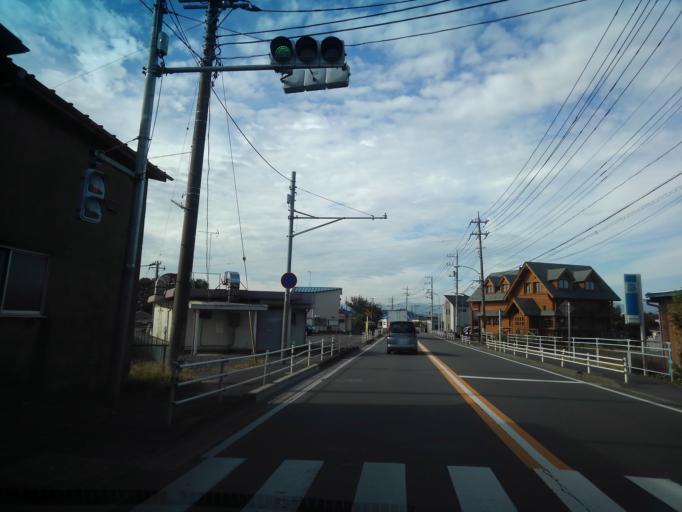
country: JP
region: Tokyo
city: Fussa
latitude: 35.7756
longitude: 139.3508
